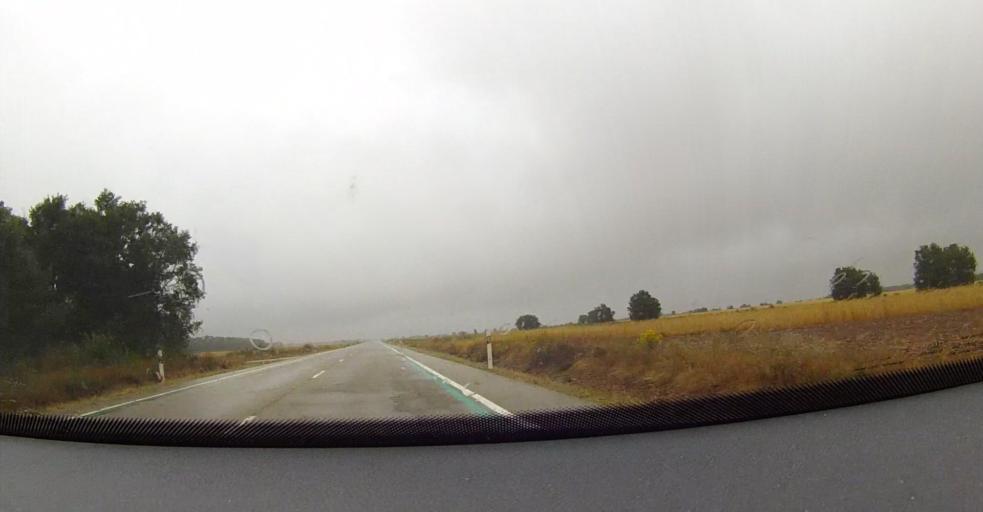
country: ES
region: Castille and Leon
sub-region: Provincia de Palencia
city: Poza de la Vega
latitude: 42.5946
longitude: -4.7621
